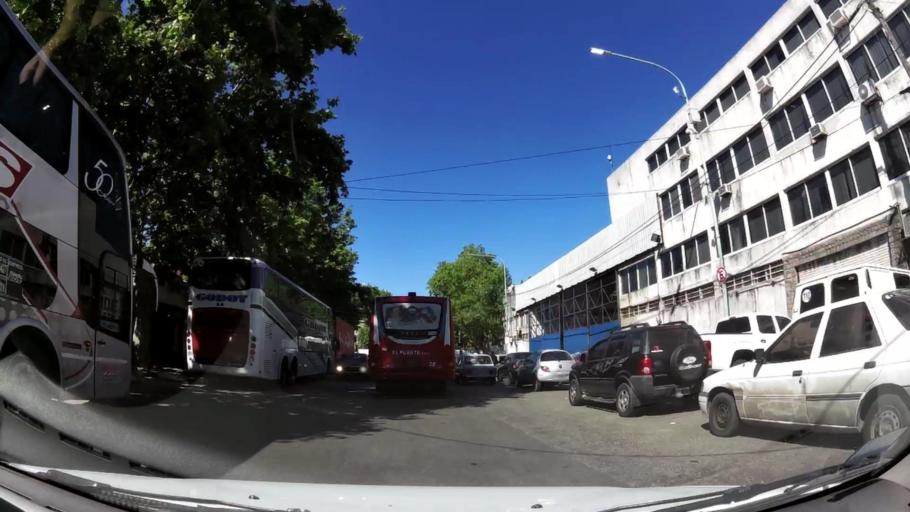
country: AR
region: Buenos Aires F.D.
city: Retiro
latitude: -34.5826
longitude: -58.3768
